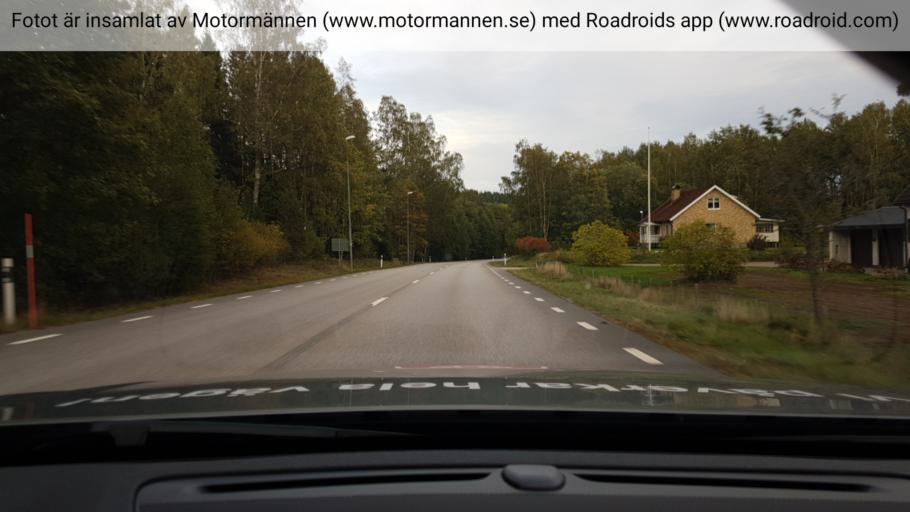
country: SE
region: Vaestra Goetaland
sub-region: Bengtsfors Kommun
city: Dals Langed
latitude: 59.0579
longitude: 12.4561
